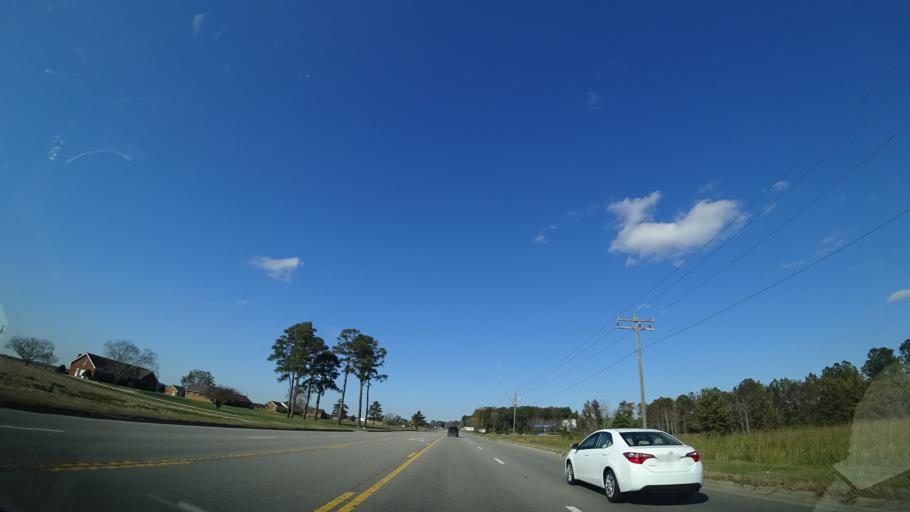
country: US
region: North Carolina
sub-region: Currituck County
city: Moyock
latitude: 36.5347
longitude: -76.1854
